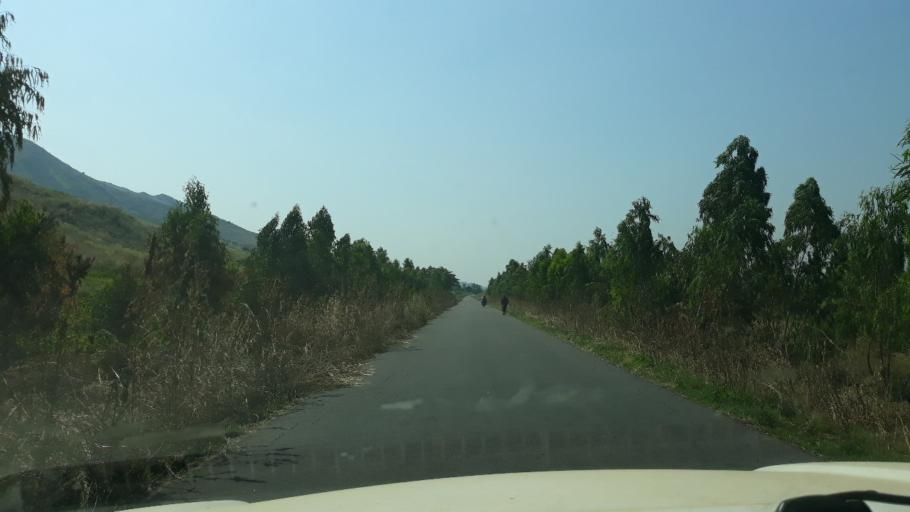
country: CD
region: South Kivu
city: Uvira
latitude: -3.2639
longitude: 29.1614
